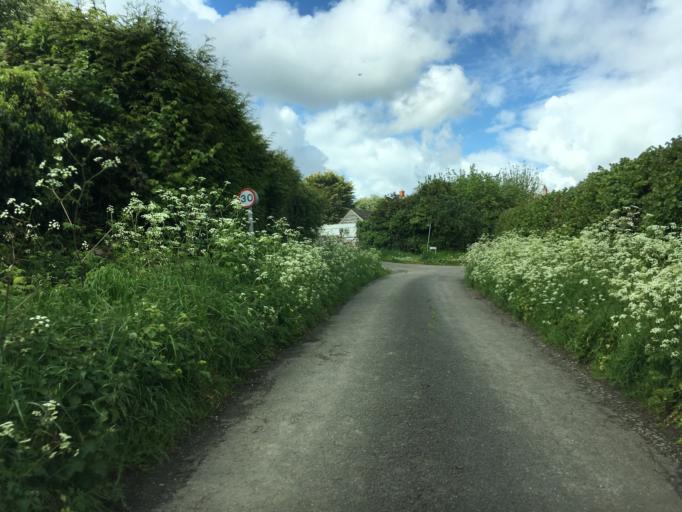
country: GB
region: England
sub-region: Gloucestershire
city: Stonehouse
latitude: 51.7738
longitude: -2.3234
